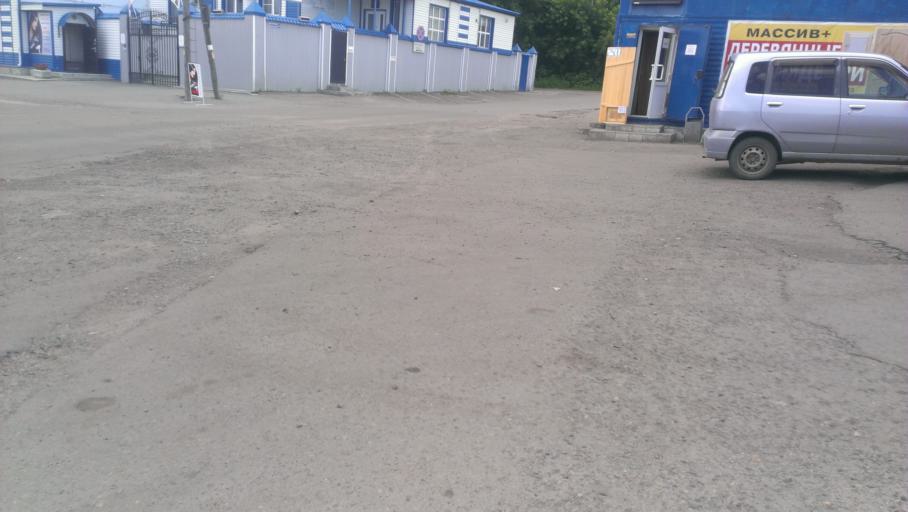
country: RU
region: Altai Krai
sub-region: Gorod Barnaulskiy
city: Barnaul
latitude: 53.3375
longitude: 83.7309
